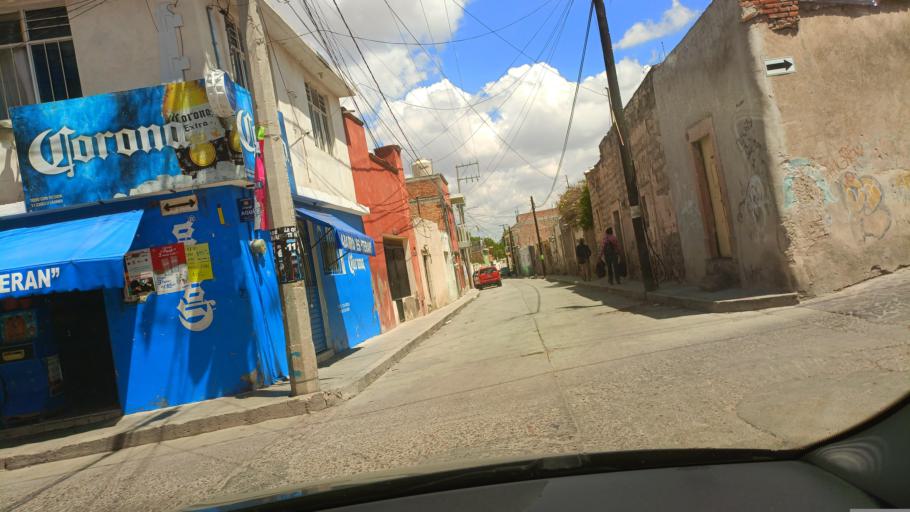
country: MX
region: Guanajuato
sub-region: San Luis de la Paz
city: San Luis de la Paz
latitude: 21.3041
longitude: -100.5165
